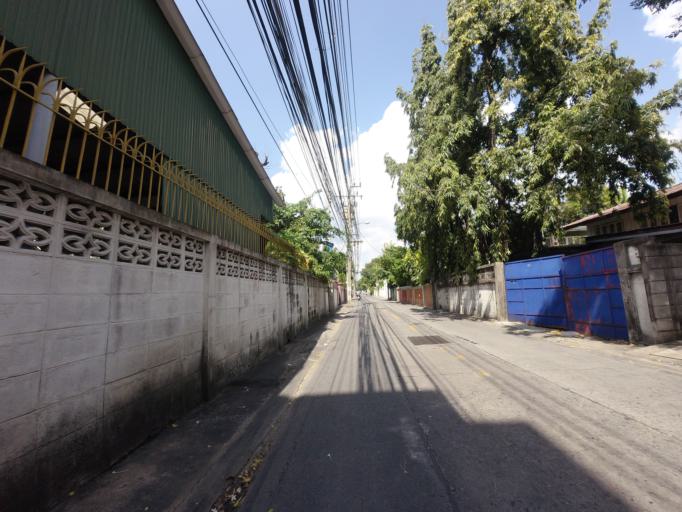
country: TH
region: Bangkok
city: Phaya Thai
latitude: 13.7916
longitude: 100.5552
